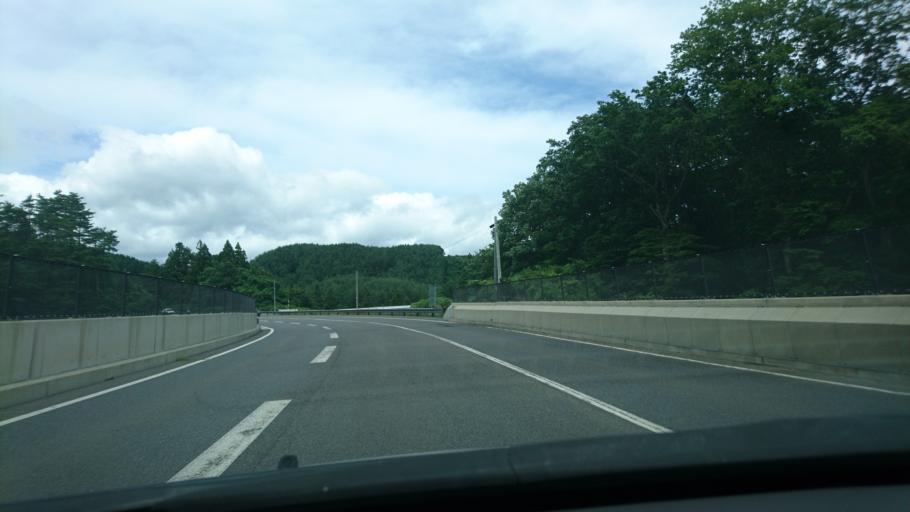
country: JP
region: Aomori
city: Hachinohe
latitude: 40.2376
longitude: 141.7824
